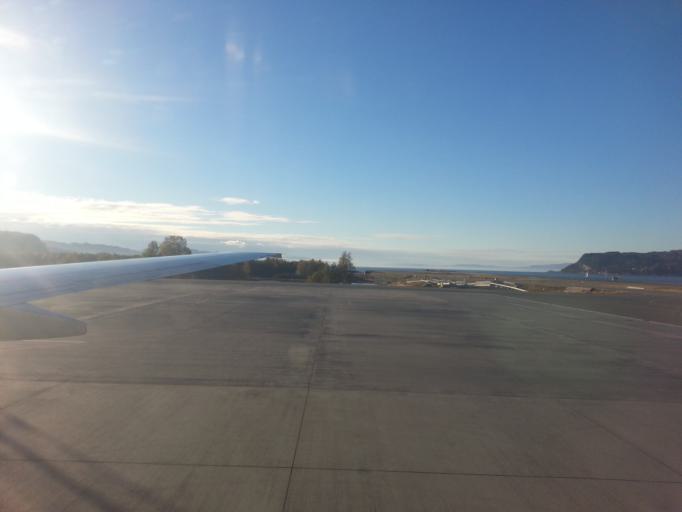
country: NO
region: Nord-Trondelag
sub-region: Stjordal
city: Stjordal
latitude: 63.4551
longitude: 10.9135
